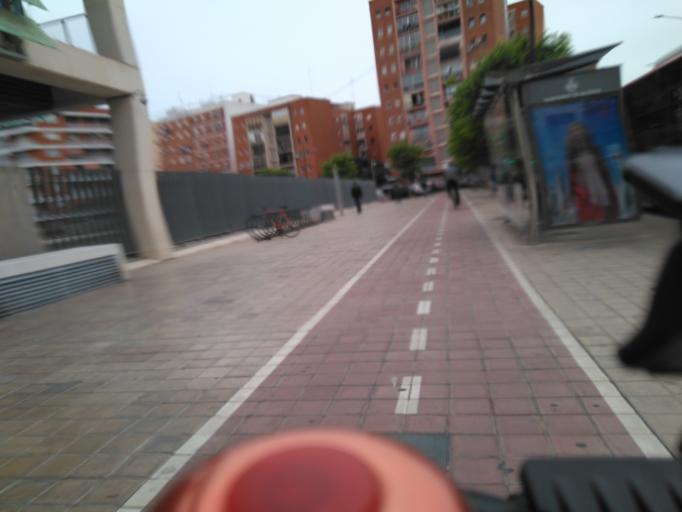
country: ES
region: Valencia
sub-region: Provincia de Valencia
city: Mislata
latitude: 39.4711
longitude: -0.4051
